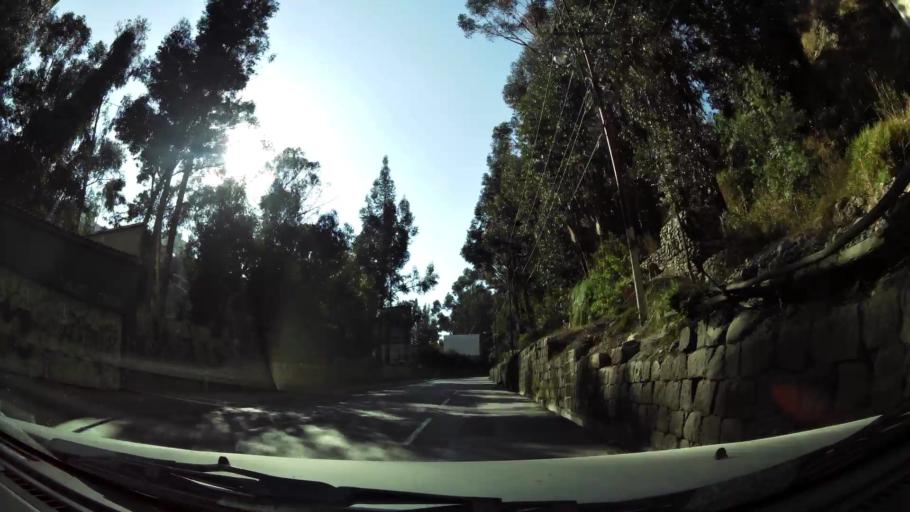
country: BO
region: La Paz
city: La Paz
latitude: -16.5158
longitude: -68.1172
